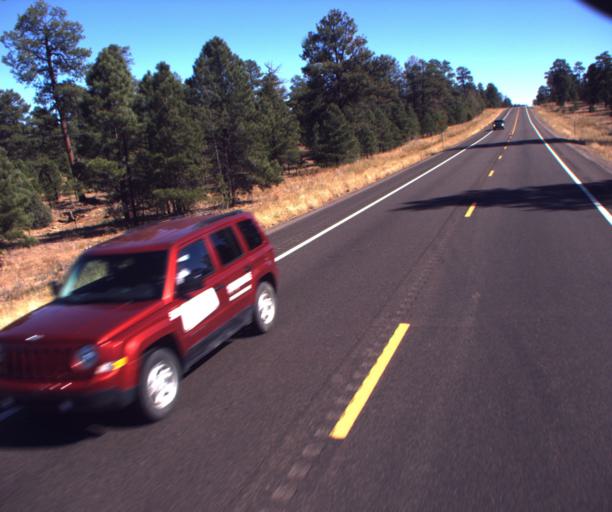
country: US
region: Arizona
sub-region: Apache County
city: Saint Michaels
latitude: 35.7016
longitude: -109.2954
